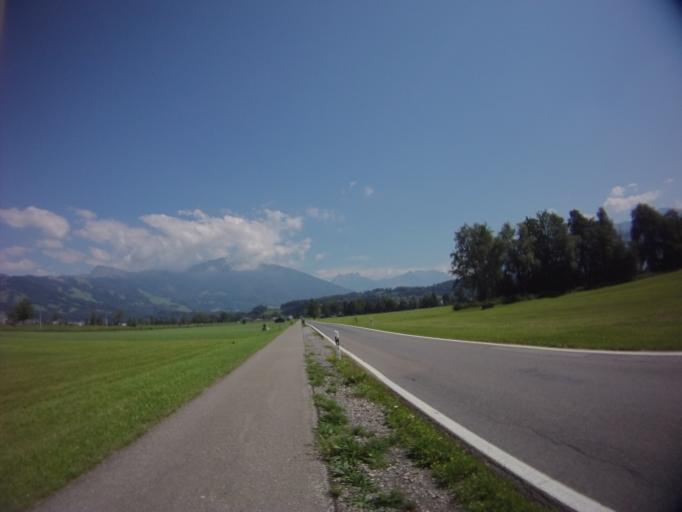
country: CH
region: Saint Gallen
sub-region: Wahlkreis See-Gaster
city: Uznach
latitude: 47.2146
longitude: 8.9938
